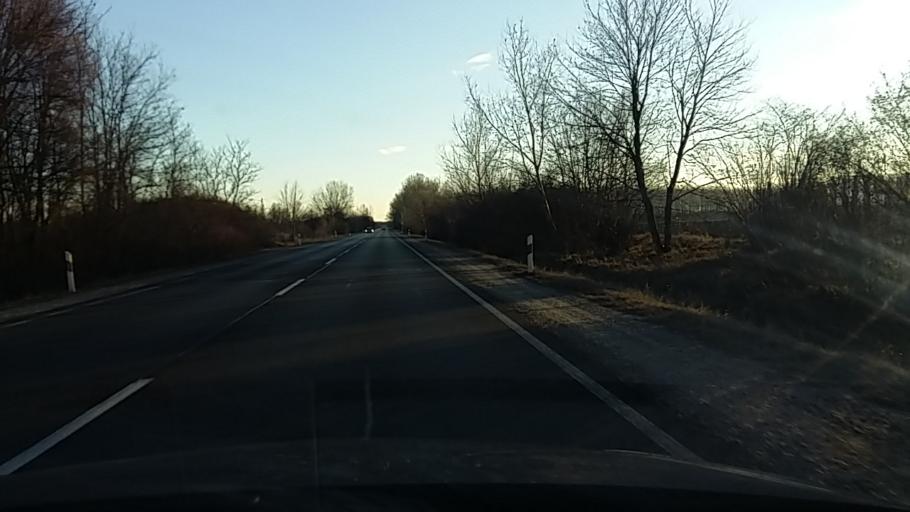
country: HU
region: Szabolcs-Szatmar-Bereg
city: Ujfeherto
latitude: 47.8456
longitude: 21.7044
